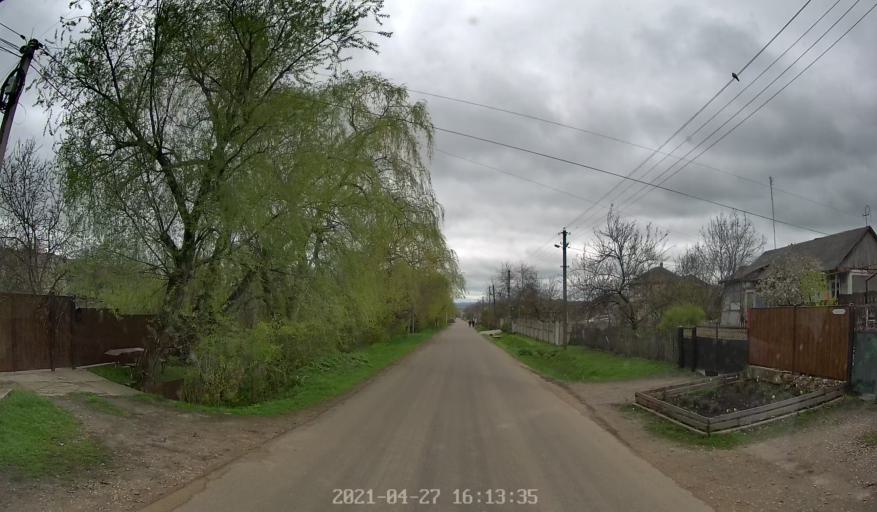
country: MD
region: Chisinau
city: Vadul lui Voda
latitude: 47.0080
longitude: 29.0129
